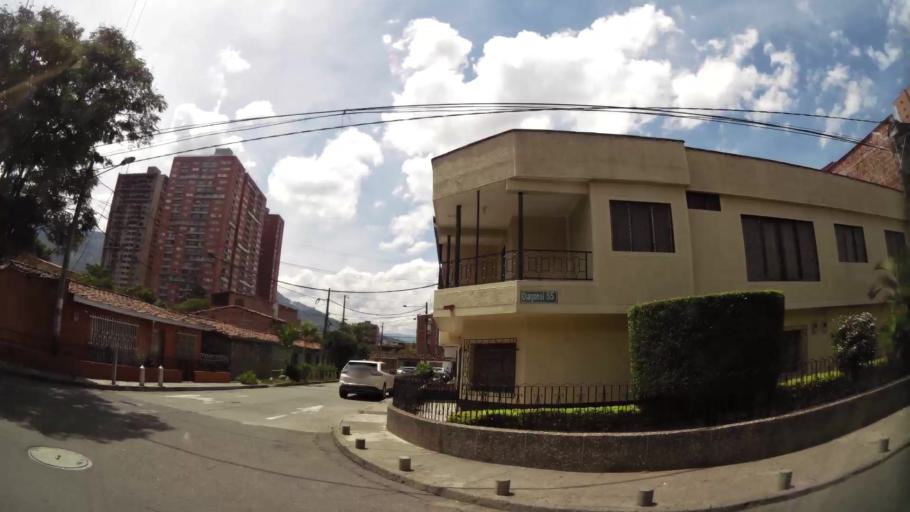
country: CO
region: Antioquia
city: Bello
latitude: 6.3390
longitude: -75.5508
